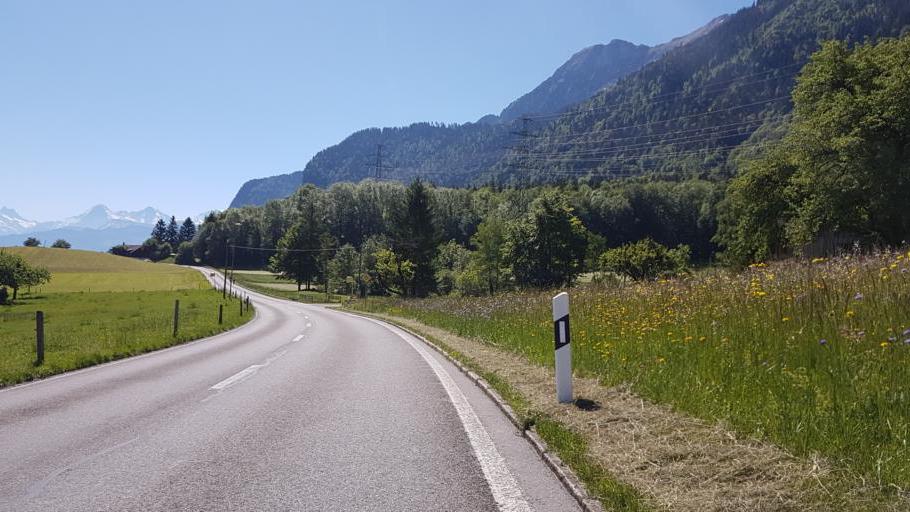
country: CH
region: Bern
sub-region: Thun District
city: Blumenstein
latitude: 46.7200
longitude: 7.5429
